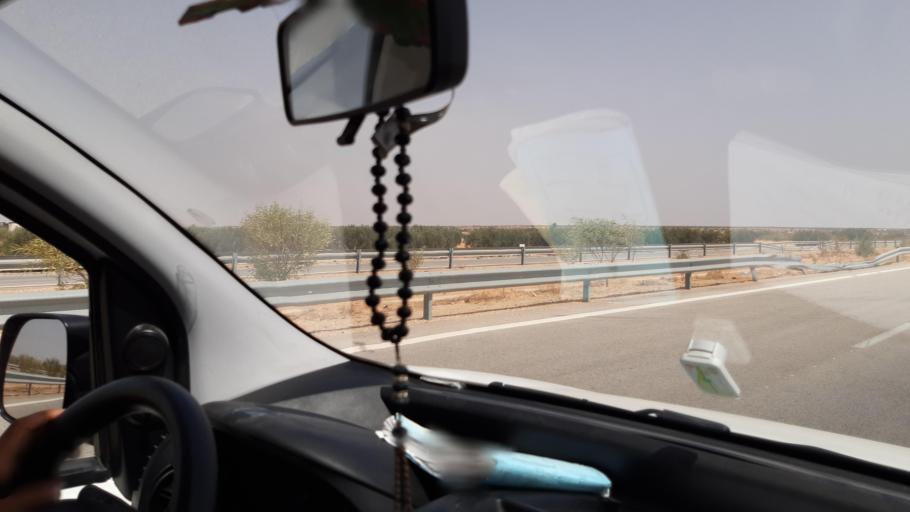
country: TN
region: Safaqis
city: Bi'r `Ali Bin Khalifah
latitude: 34.5254
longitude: 10.1340
